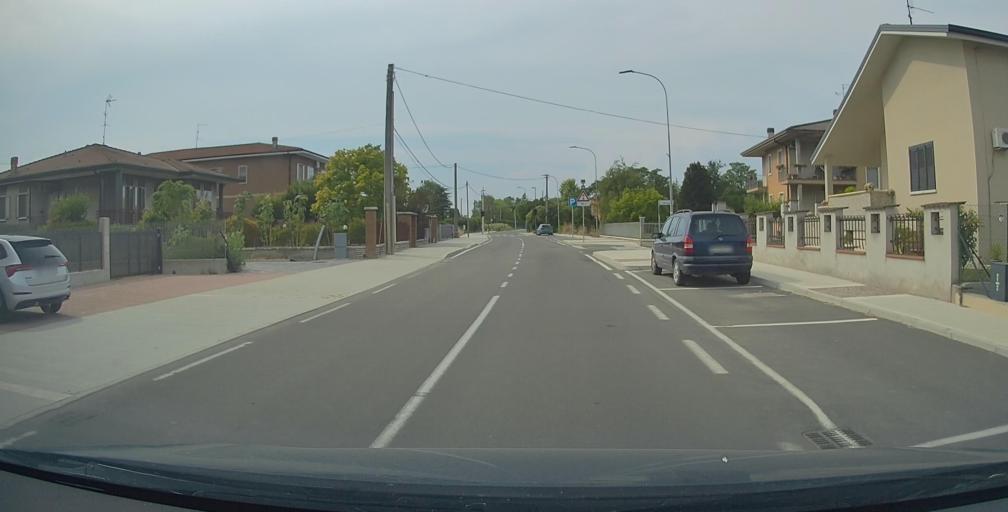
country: IT
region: Veneto
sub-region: Provincia di Verona
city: Pradelle
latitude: 45.2860
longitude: 10.8664
